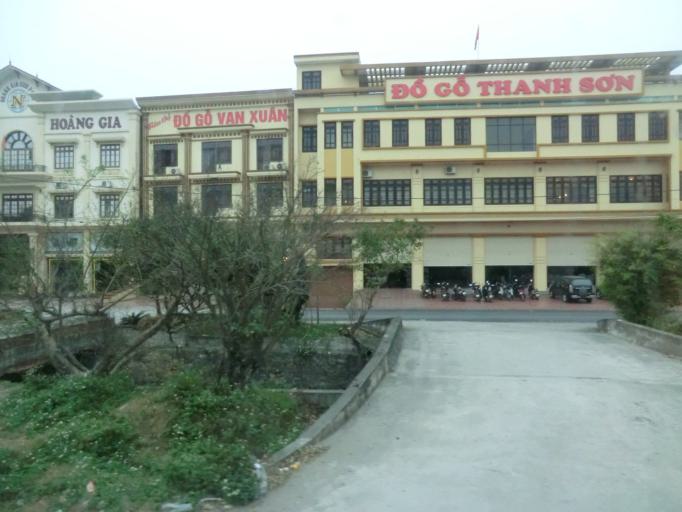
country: VN
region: Nam Dinh
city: Thi Tran Lam
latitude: 20.3118
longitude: 106.0440
